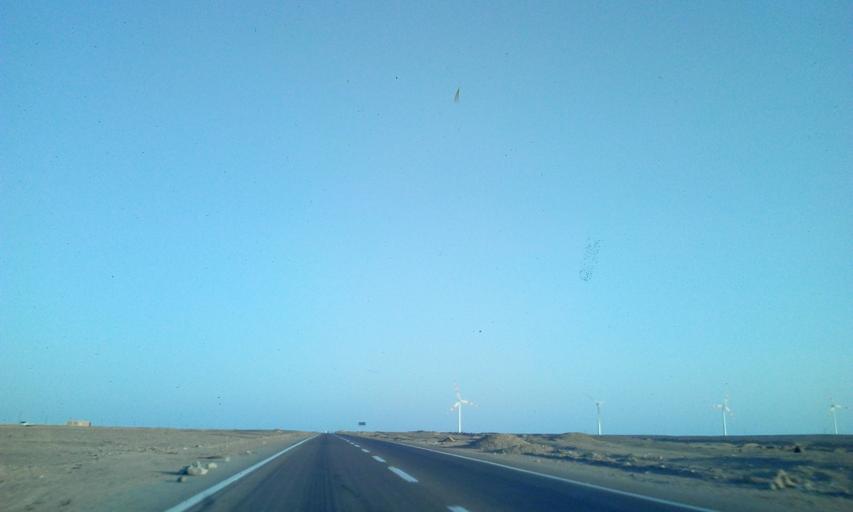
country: EG
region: South Sinai
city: Tor
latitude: 28.0715
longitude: 33.2611
